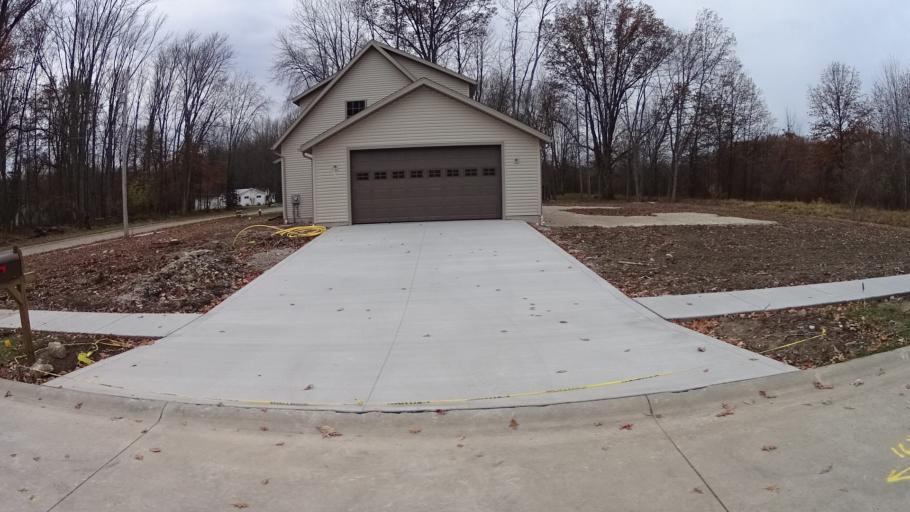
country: US
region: Ohio
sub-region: Lorain County
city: North Ridgeville
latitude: 41.3882
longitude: -82.0638
